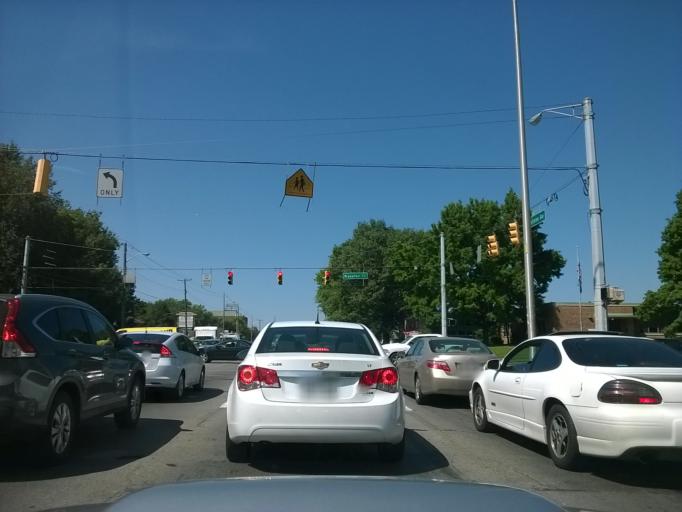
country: US
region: Indiana
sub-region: Marion County
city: Broad Ripple
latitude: 39.8621
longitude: -86.1221
